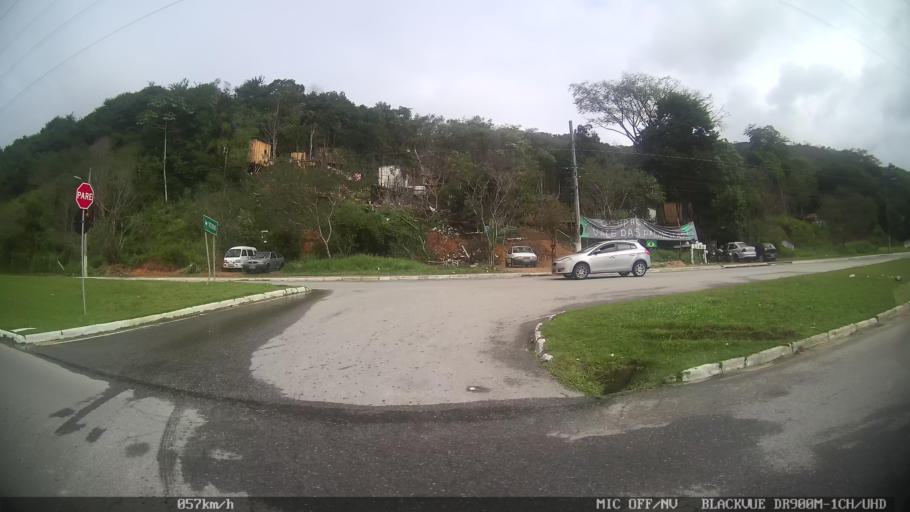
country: BR
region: Santa Catarina
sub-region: Biguacu
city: Biguacu
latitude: -27.5468
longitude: -48.6472
